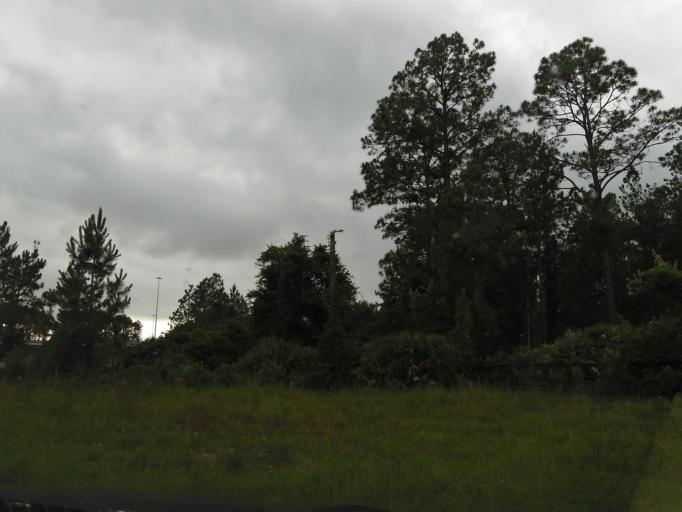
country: US
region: Florida
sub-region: Baker County
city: Macclenny
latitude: 30.2410
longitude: -82.3021
